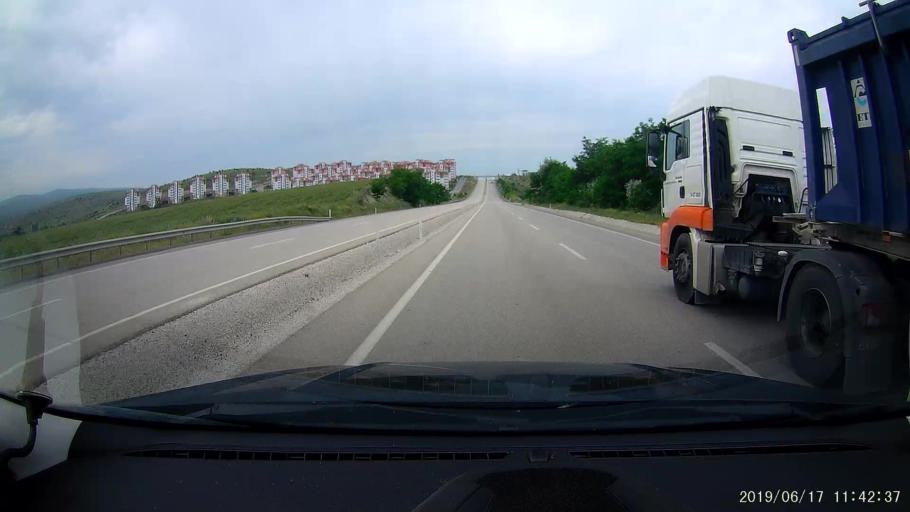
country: TR
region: Cankiri
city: Kursunlu
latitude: 40.8371
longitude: 33.2963
